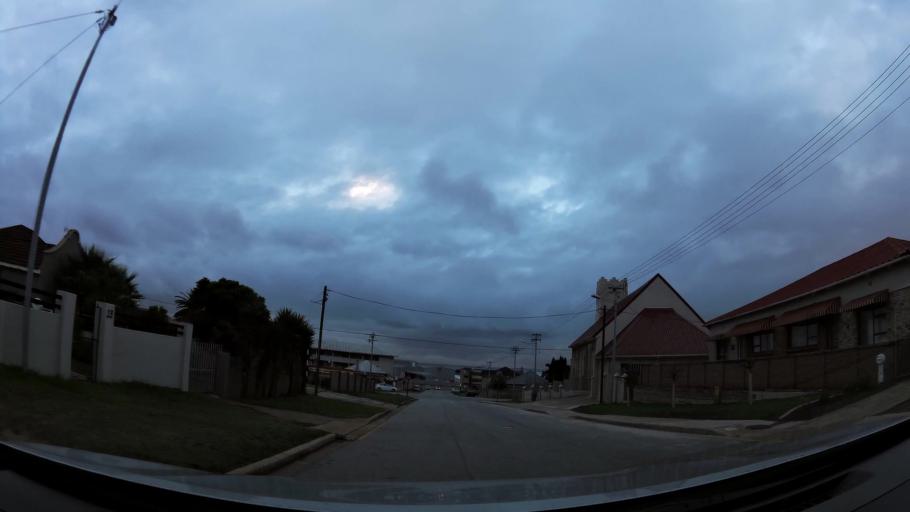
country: ZA
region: Eastern Cape
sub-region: Nelson Mandela Bay Metropolitan Municipality
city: Port Elizabeth
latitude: -33.9300
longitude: 25.5991
